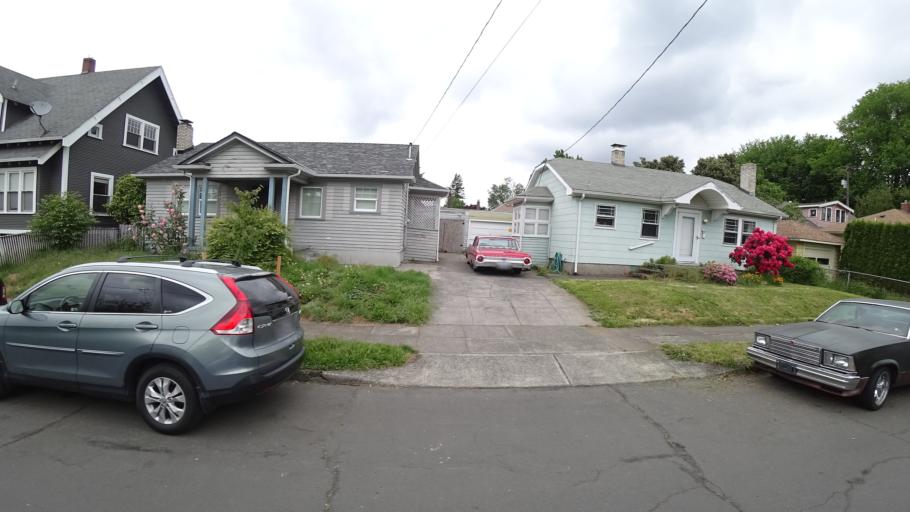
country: US
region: Oregon
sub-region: Multnomah County
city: Portland
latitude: 45.5055
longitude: -122.6211
